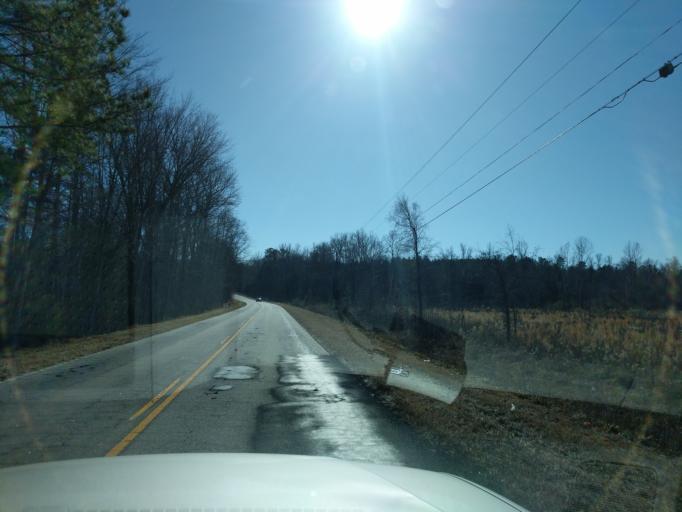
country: US
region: South Carolina
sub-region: Laurens County
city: Clinton
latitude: 34.5014
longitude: -81.8907
